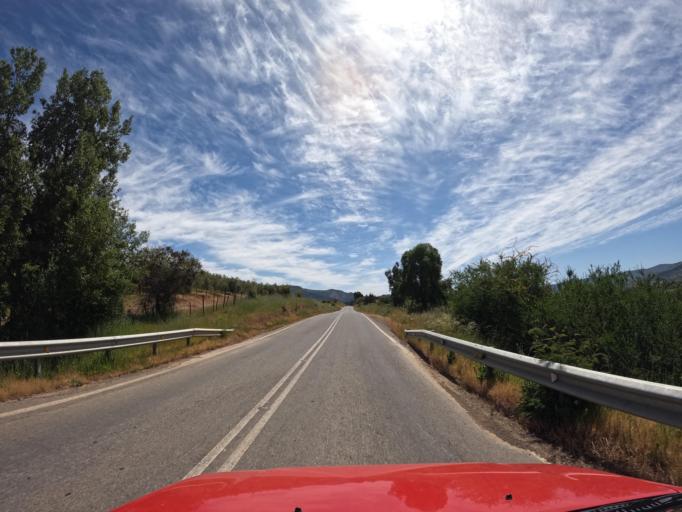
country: CL
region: Maule
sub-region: Provincia de Talca
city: Talca
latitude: -35.0162
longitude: -71.7737
